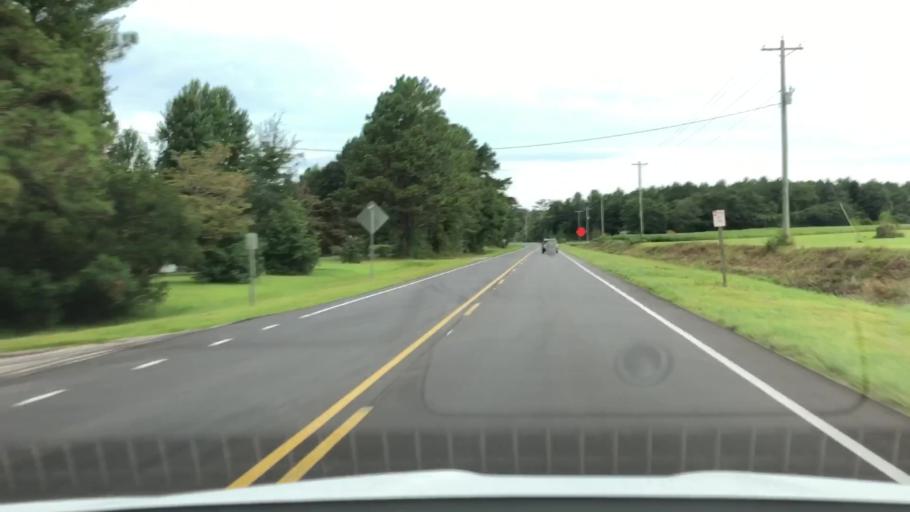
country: US
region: North Carolina
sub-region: Jones County
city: Maysville
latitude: 34.8678
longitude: -77.1934
